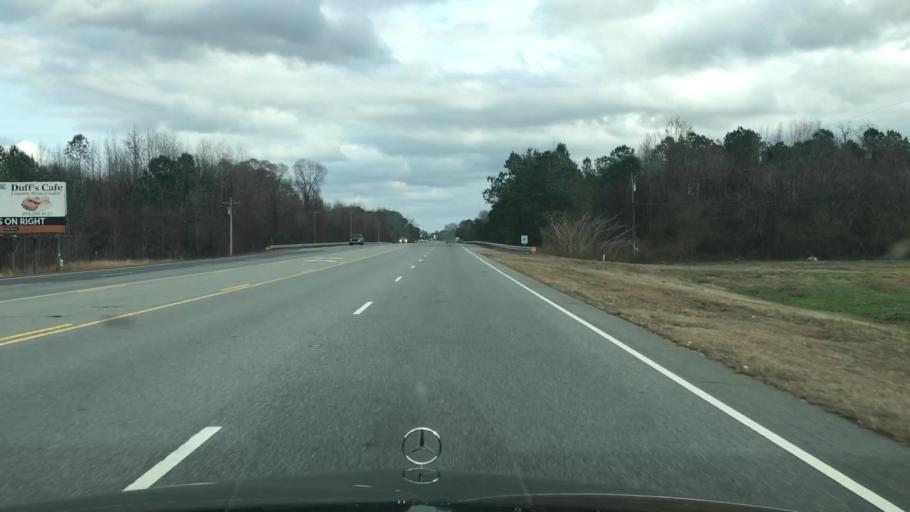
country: US
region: North Carolina
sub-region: Duplin County
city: Beulaville
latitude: 34.9284
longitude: -77.8051
